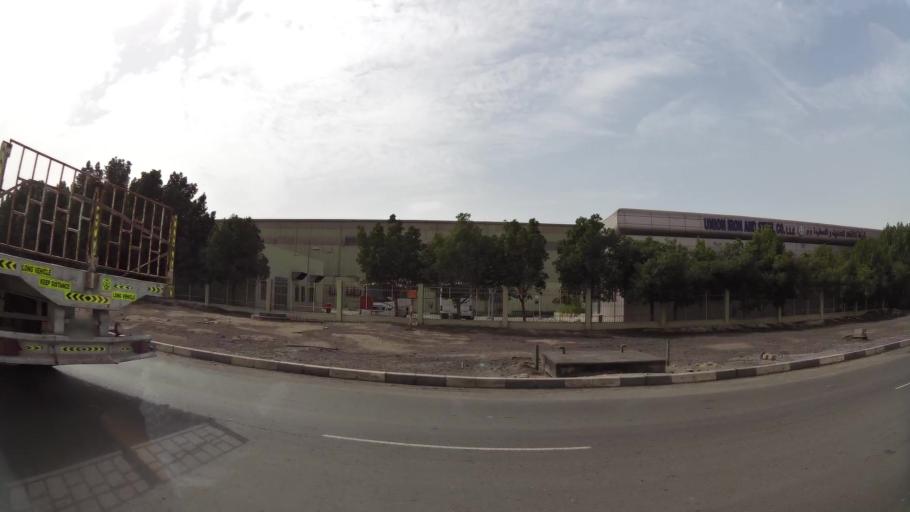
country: AE
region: Abu Dhabi
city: Abu Dhabi
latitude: 24.3266
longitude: 54.4737
